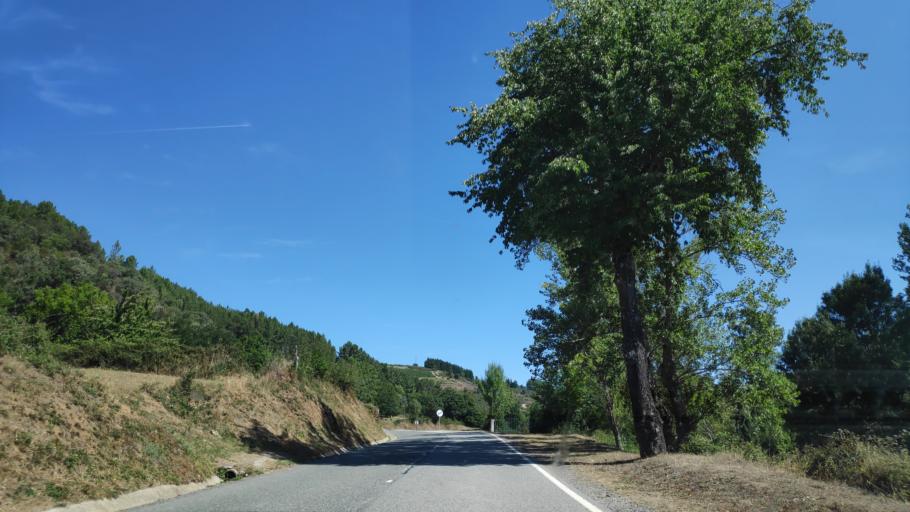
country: PT
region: Braganca
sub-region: Braganca Municipality
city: Braganca
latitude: 41.8764
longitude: -6.7447
